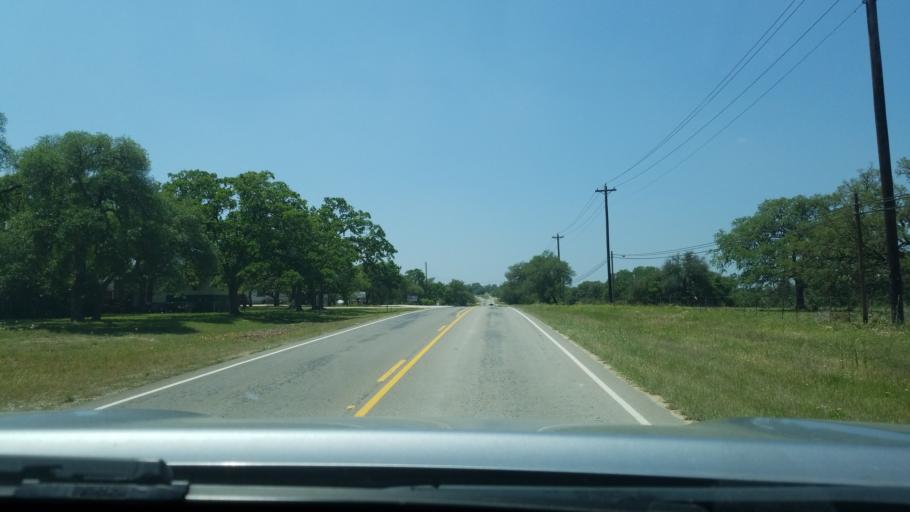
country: US
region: Texas
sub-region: Blanco County
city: Blanco
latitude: 30.0683
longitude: -98.4013
